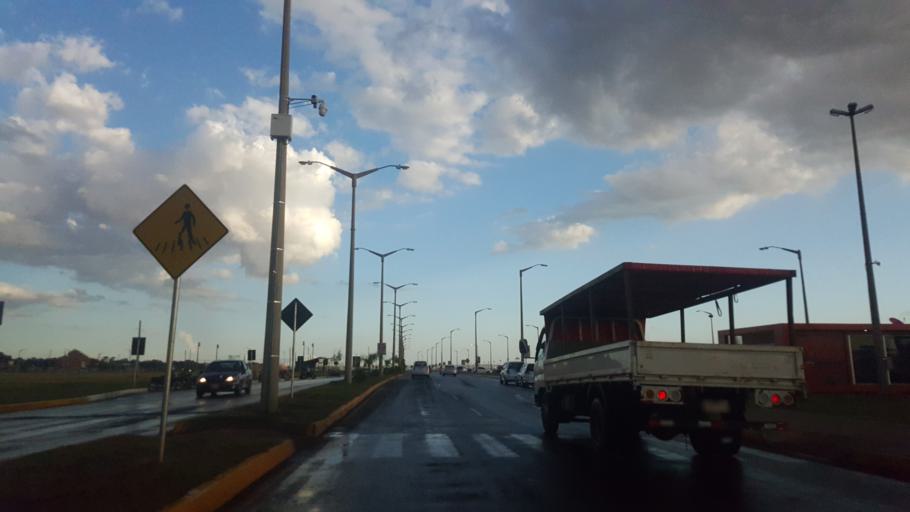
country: PY
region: Itapua
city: Encarnacion
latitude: -27.3374
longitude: -55.8721
